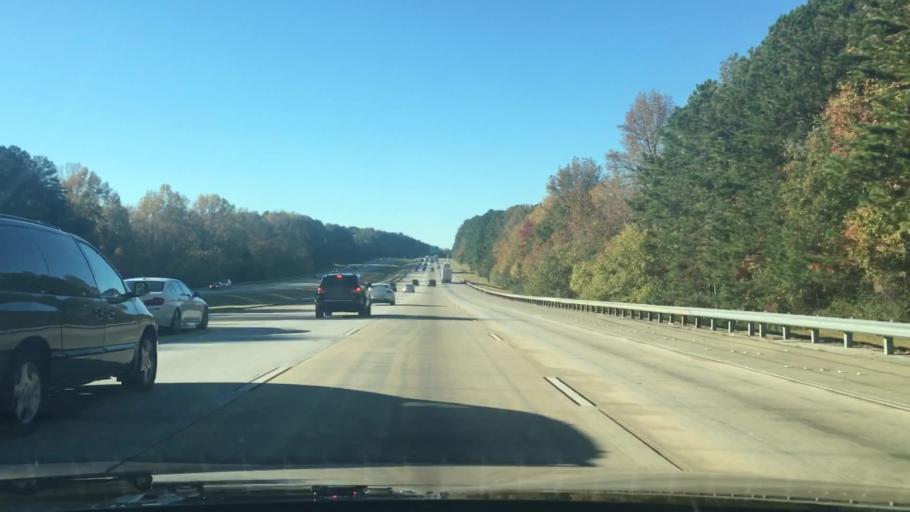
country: US
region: Georgia
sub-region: Fulton County
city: Palmetto
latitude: 33.4629
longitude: -84.6732
